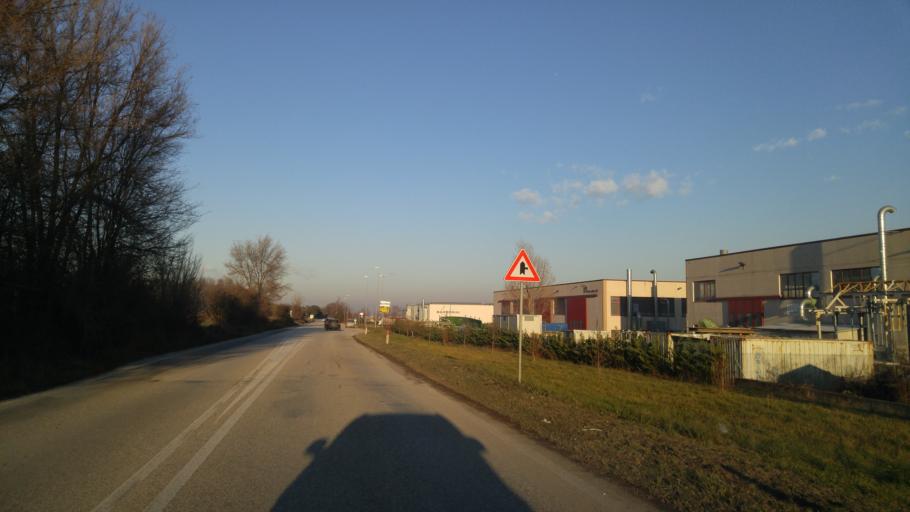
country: IT
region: The Marches
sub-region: Provincia di Pesaro e Urbino
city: Monte Porzio
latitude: 43.7035
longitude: 13.0664
